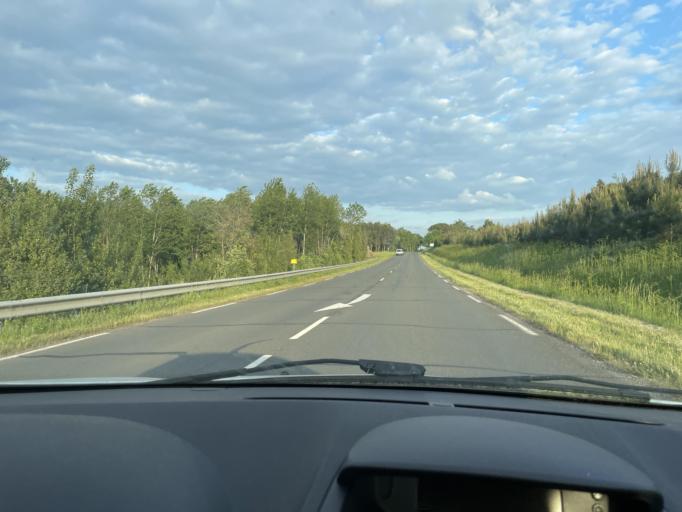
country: FR
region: Aquitaine
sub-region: Departement du Lot-et-Garonne
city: Casteljaloux
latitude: 44.3472
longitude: 0.0353
